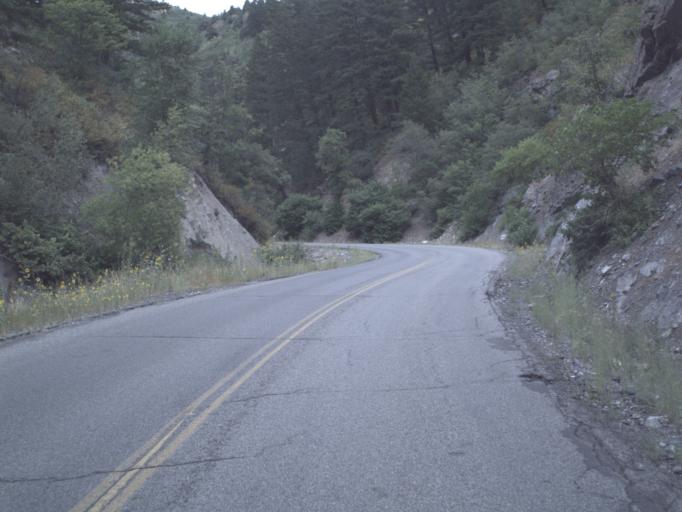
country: US
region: Utah
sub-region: Utah County
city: Orem
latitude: 40.3754
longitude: -111.5683
